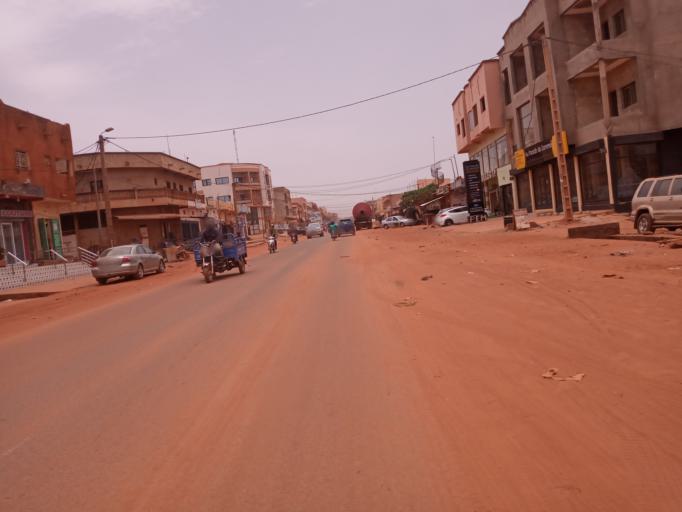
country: ML
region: Bamako
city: Bamako
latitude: 12.5813
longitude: -8.0196
